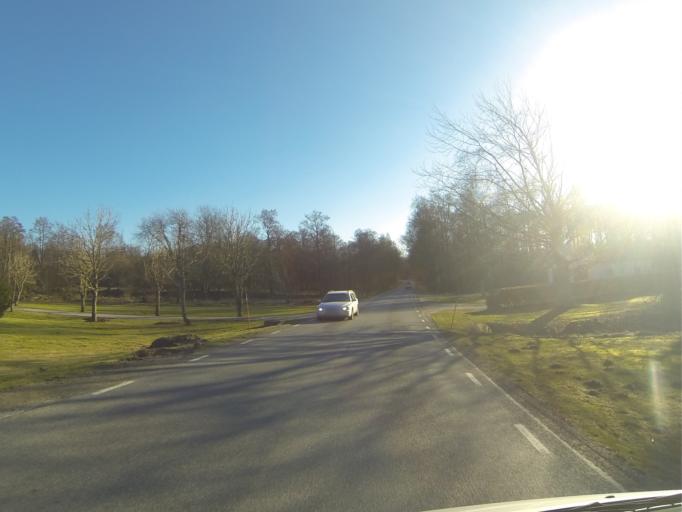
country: SE
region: Skane
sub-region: Horby Kommun
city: Hoerby
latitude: 55.8898
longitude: 13.6669
